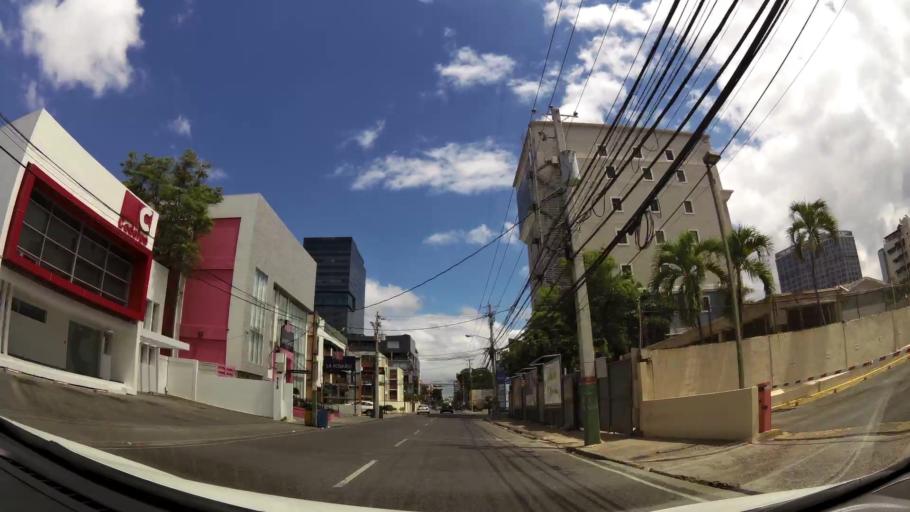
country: DO
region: Nacional
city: La Julia
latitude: 18.4711
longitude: -69.9430
